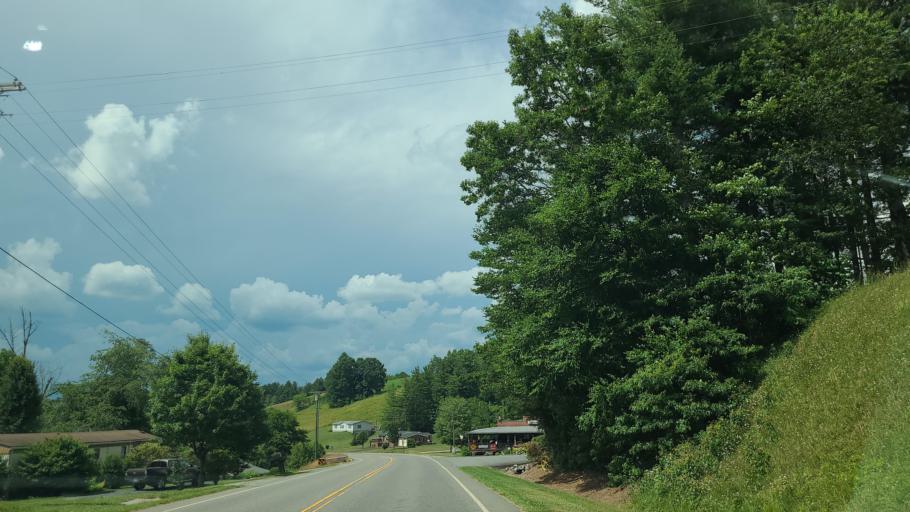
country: US
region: North Carolina
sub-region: Ashe County
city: Jefferson
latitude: 36.3562
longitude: -81.3861
